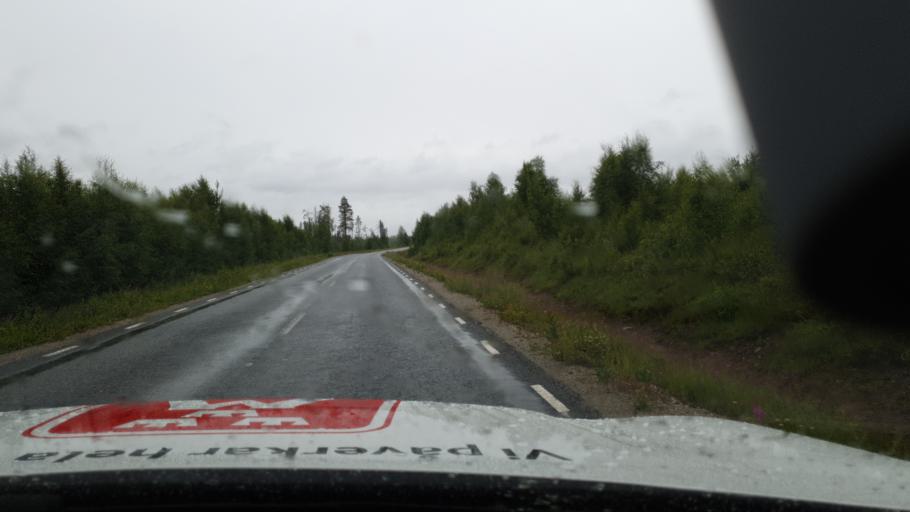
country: SE
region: Vaesterbotten
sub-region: Vindelns Kommun
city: Vindeln
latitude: 64.4656
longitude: 19.7615
